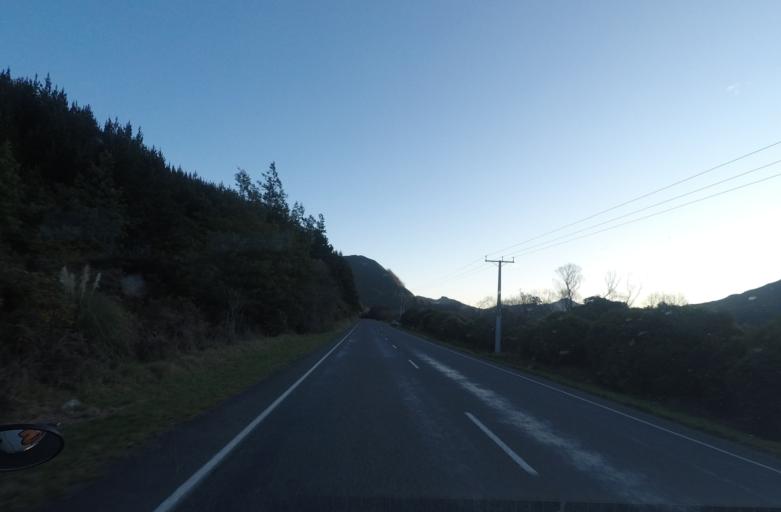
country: NZ
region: Marlborough
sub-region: Marlborough District
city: Picton
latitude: -41.2839
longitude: 173.7153
